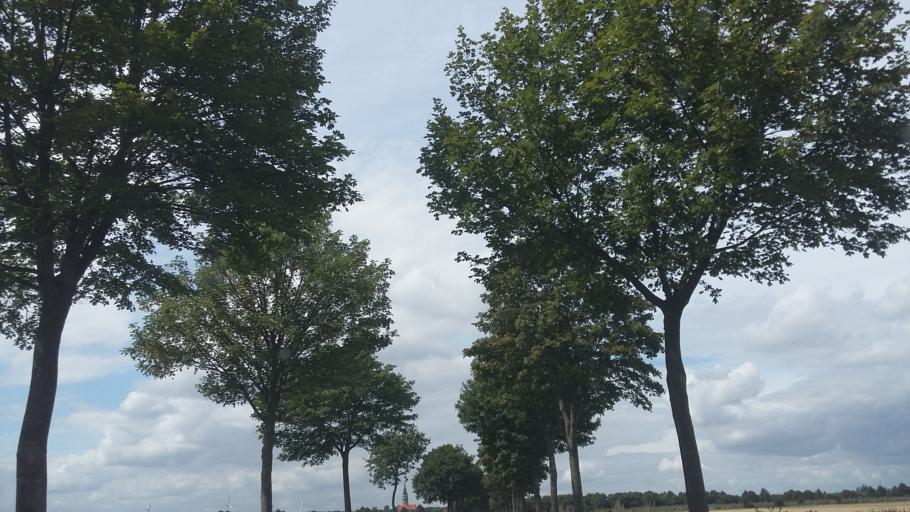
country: DE
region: Lower Saxony
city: Harsum
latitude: 52.2067
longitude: 9.9835
